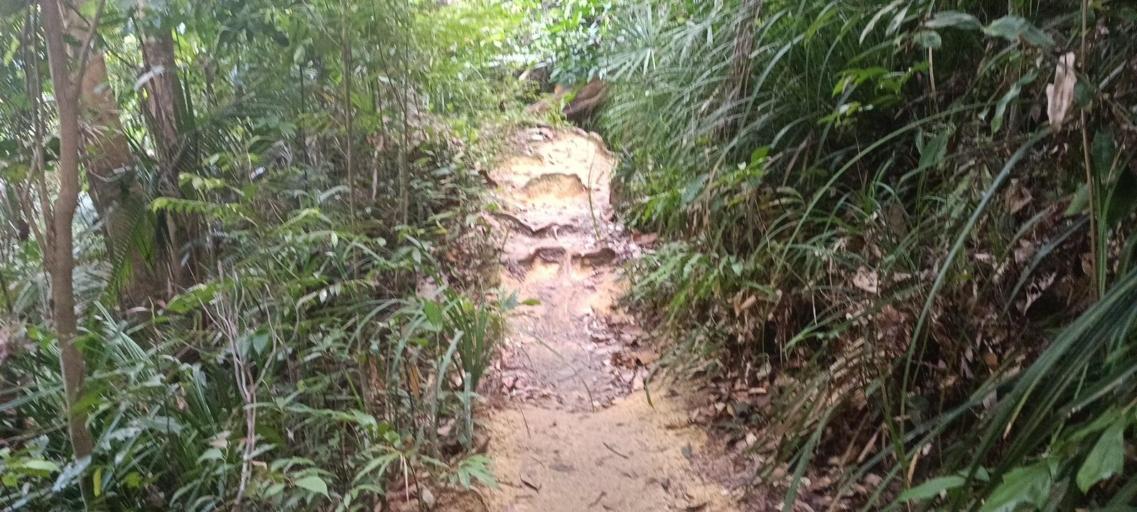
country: MY
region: Penang
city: Tanjung Tokong
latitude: 5.4229
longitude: 100.2830
